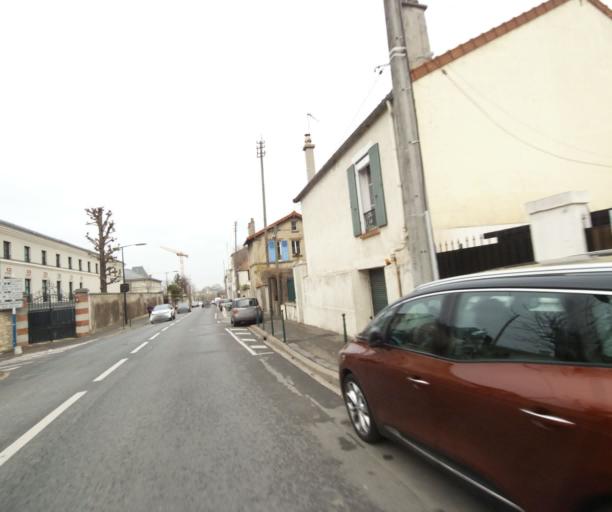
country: FR
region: Ile-de-France
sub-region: Departement des Hauts-de-Seine
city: Rueil-Malmaison
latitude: 48.8704
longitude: 2.1844
